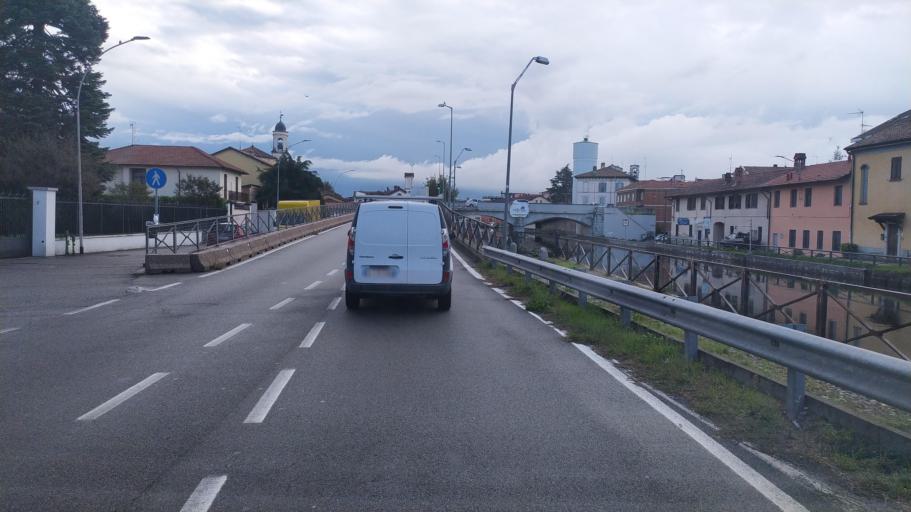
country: IT
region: Lombardy
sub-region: Citta metropolitana di Milano
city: Gaggiano
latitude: 45.4063
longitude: 9.0307
